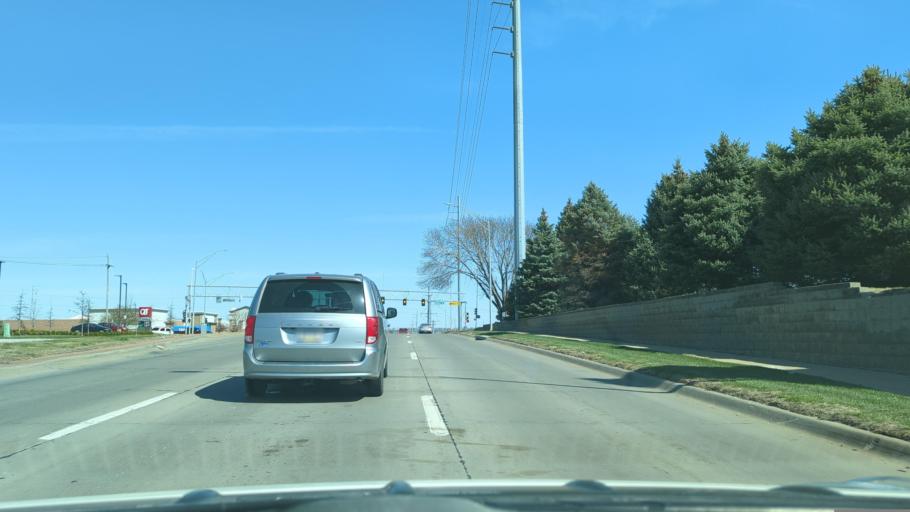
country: US
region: Nebraska
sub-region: Douglas County
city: Ralston
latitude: 41.2422
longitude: -96.0239
